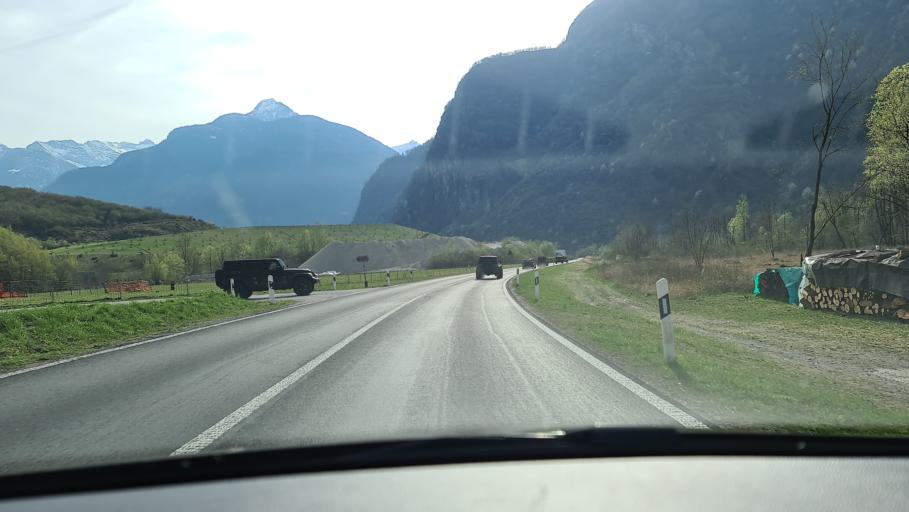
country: CH
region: Ticino
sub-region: Riviera District
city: Biasca
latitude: 46.3819
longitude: 8.9800
